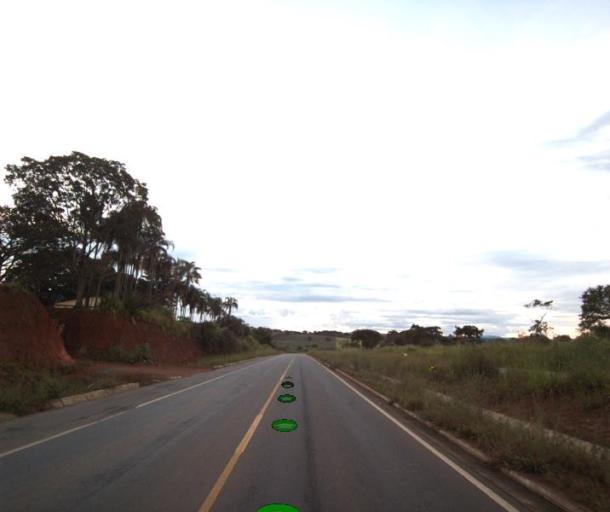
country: BR
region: Goias
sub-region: Anapolis
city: Anapolis
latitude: -16.1828
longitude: -49.0408
